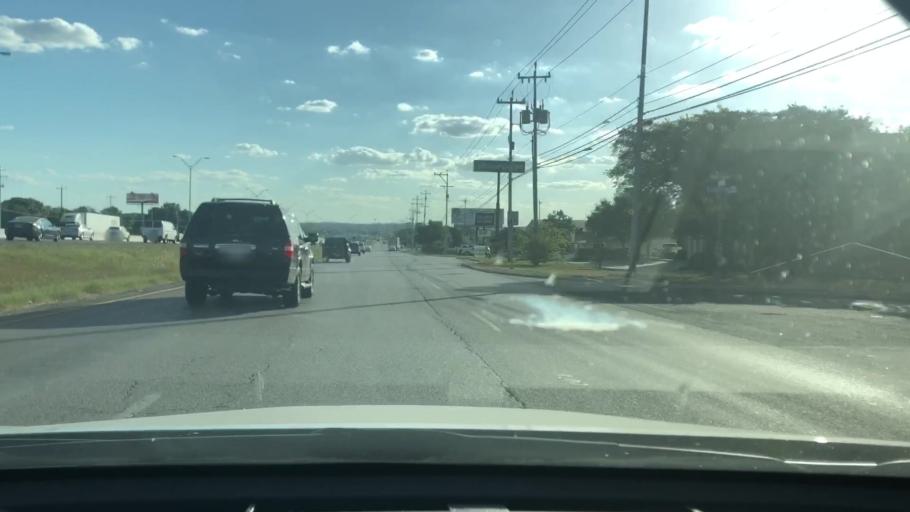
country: US
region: Texas
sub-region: Bexar County
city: Selma
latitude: 29.5975
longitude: -98.2822
